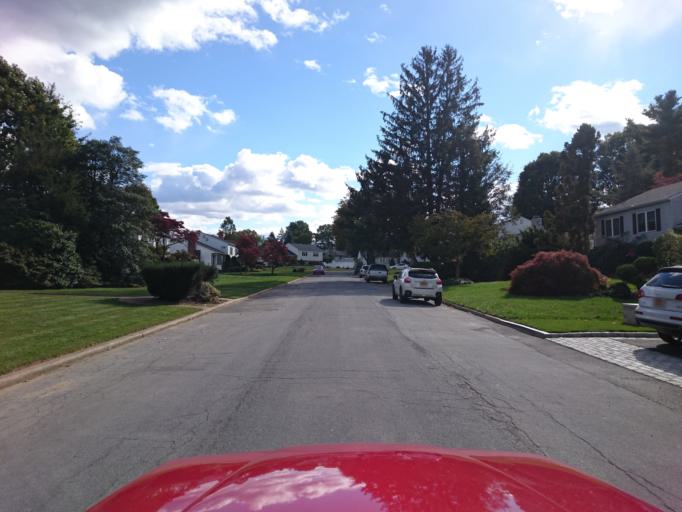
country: US
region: New York
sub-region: Nassau County
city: Glen Cove
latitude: 40.8702
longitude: -73.6451
